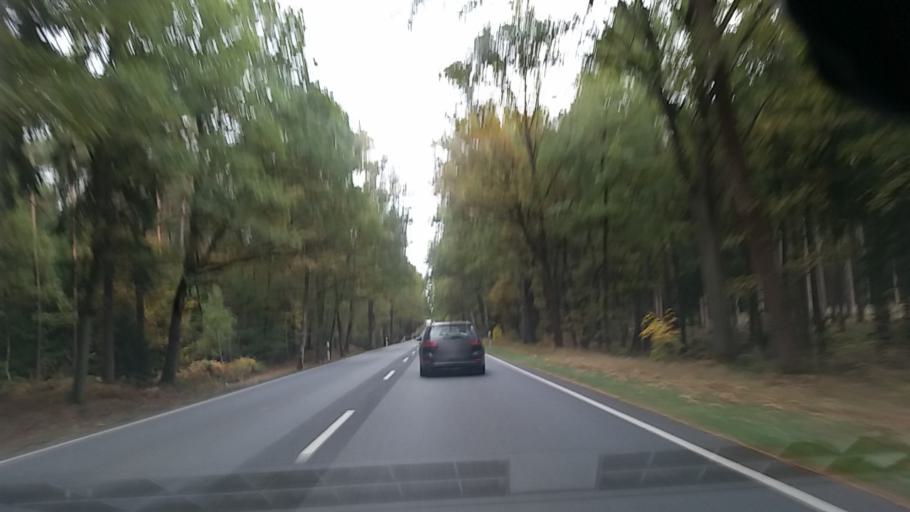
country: DE
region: Lower Saxony
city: Sprakensehl
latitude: 52.7327
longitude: 10.4855
